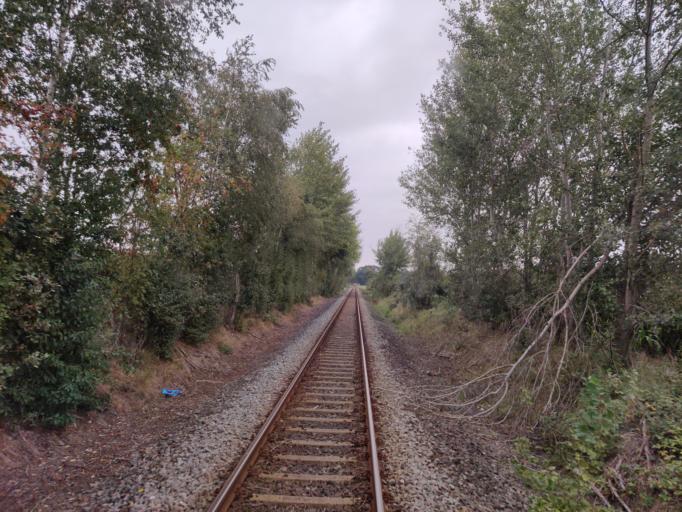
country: DE
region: Lower Saxony
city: Deinste
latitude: 53.5395
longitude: 9.4507
